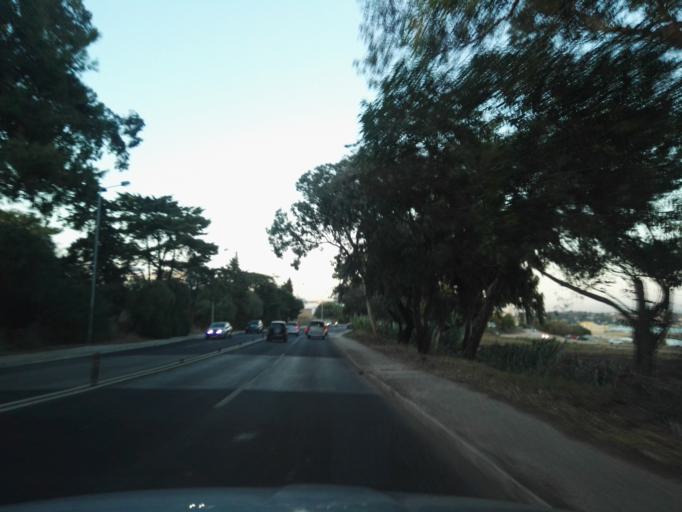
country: PT
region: Lisbon
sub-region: Oeiras
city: Oeiras
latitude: 38.6881
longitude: -9.3019
